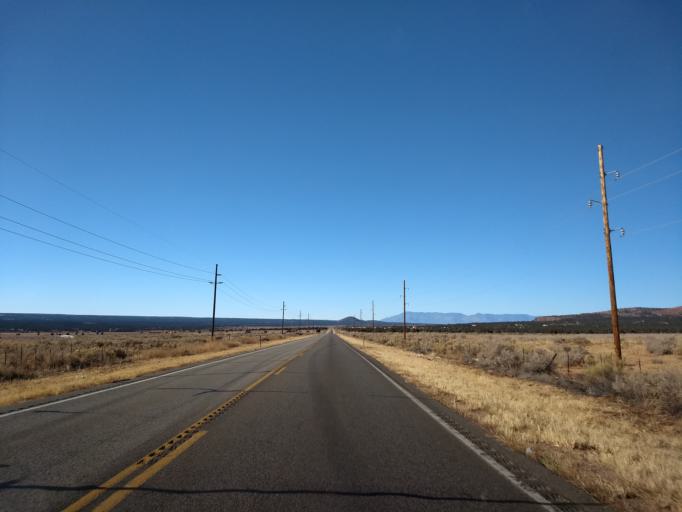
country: US
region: Arizona
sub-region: Mohave County
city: Colorado City
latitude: 37.0279
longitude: -113.0508
